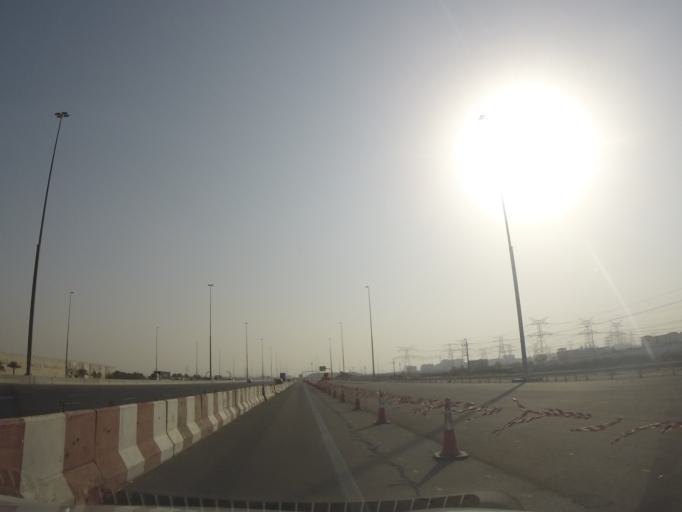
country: AE
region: Dubai
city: Dubai
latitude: 25.0312
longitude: 55.1681
